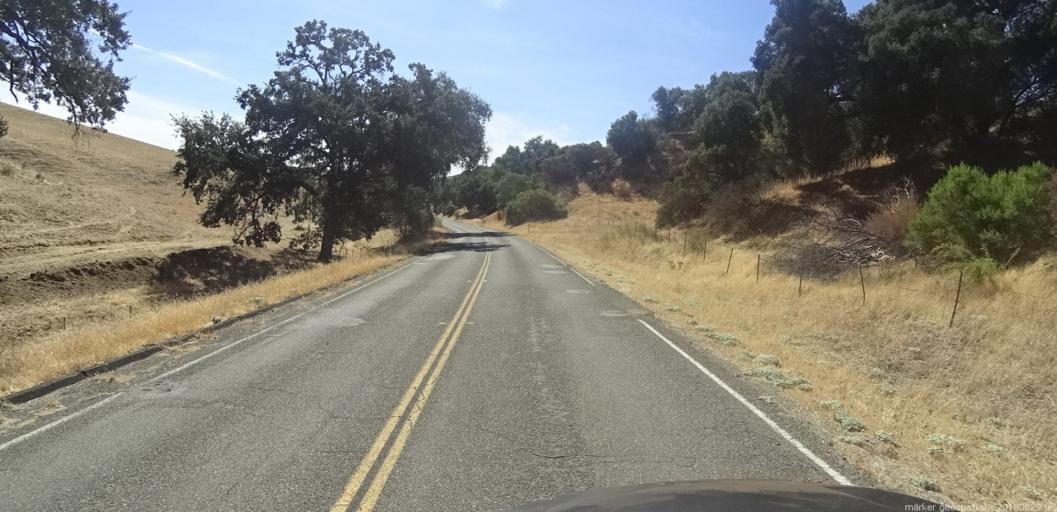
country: US
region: California
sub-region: San Luis Obispo County
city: Lake Nacimiento
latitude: 35.8416
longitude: -121.0445
